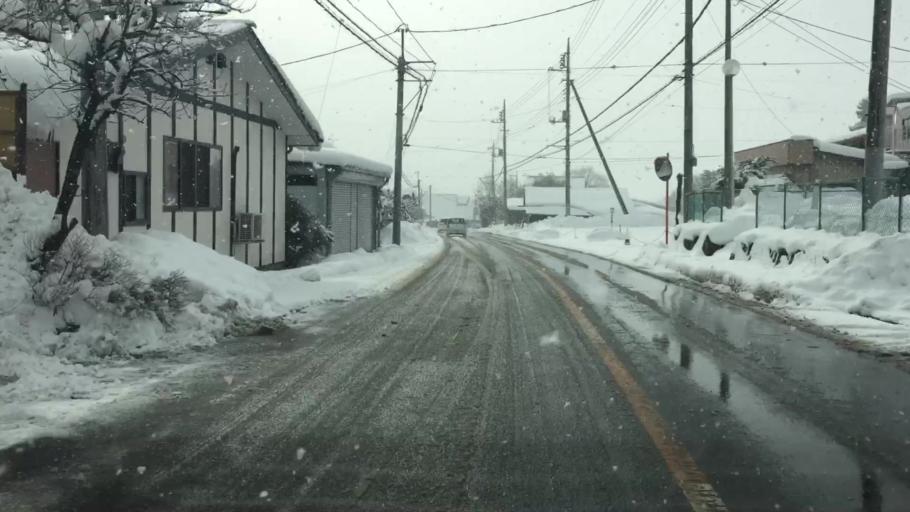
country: JP
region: Gunma
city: Numata
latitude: 36.7056
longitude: 139.0656
